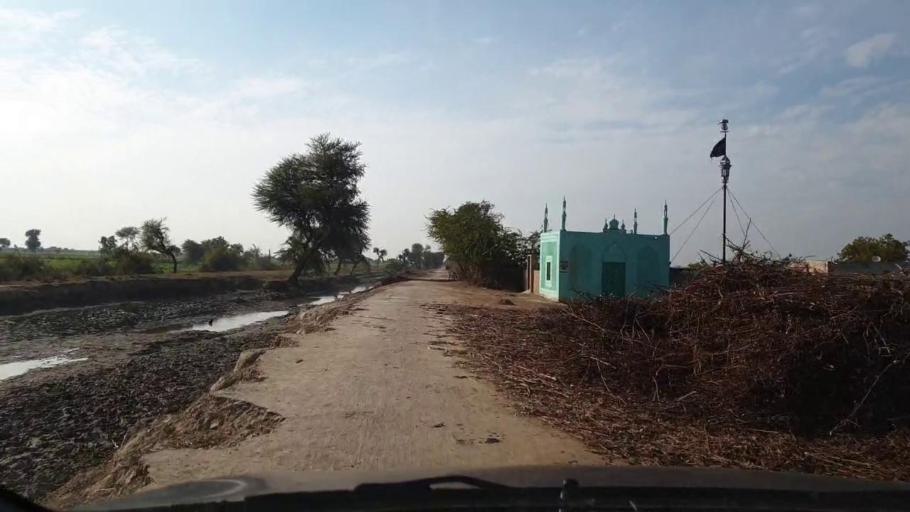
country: PK
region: Sindh
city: Sinjhoro
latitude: 25.9754
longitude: 68.8253
